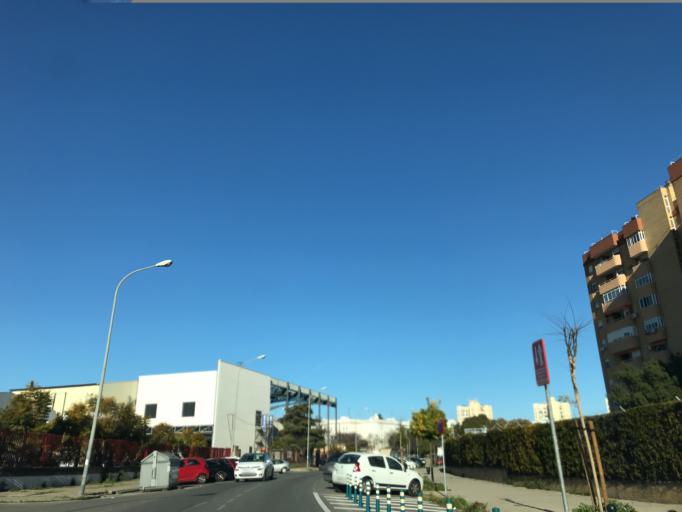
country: ES
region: Andalusia
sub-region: Provincia de Sevilla
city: Sevilla
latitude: 37.3955
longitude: -5.9550
